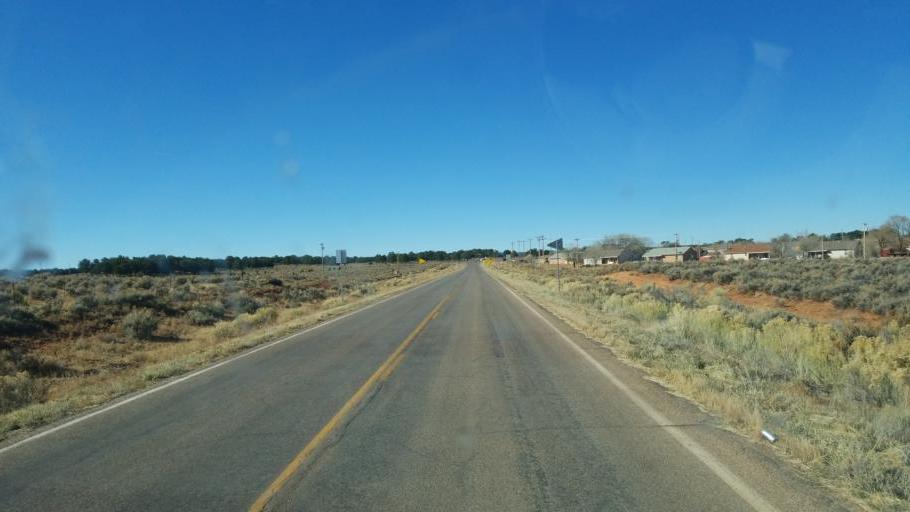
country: US
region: New Mexico
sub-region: McKinley County
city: Navajo
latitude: 36.0013
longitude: -109.0131
